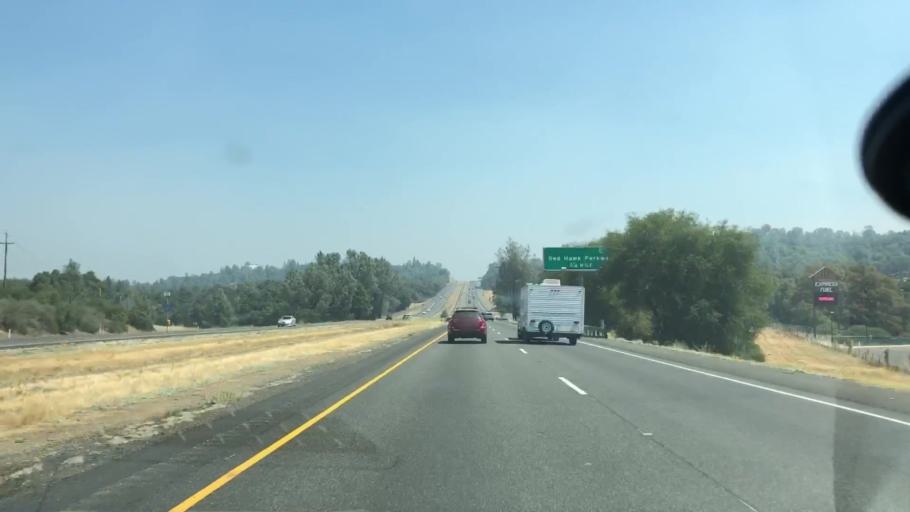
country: US
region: California
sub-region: El Dorado County
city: Shingle Springs
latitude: 38.6782
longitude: -120.9170
